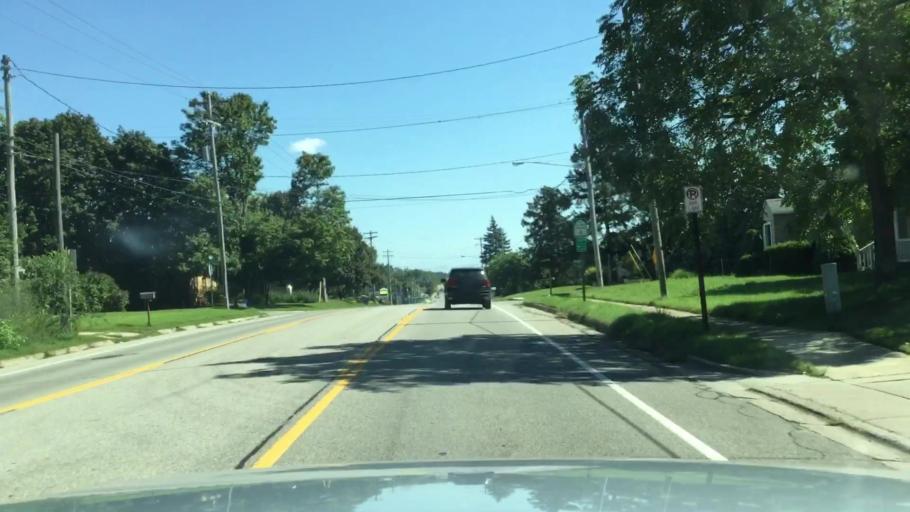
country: US
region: Michigan
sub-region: Kalamazoo County
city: Portage
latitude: 42.2155
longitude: -85.5993
